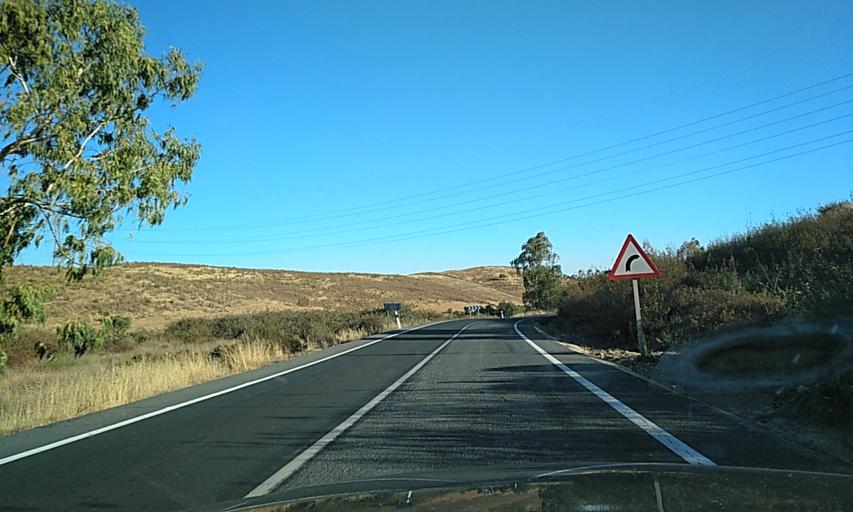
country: ES
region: Andalusia
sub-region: Provincia de Huelva
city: Alosno
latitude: 37.5154
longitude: -7.1319
